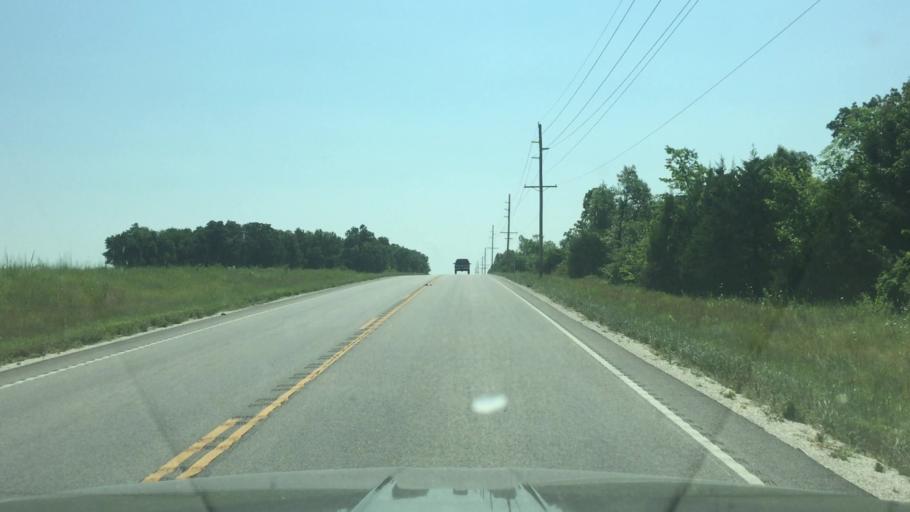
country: US
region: Missouri
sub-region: Miller County
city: Eldon
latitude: 38.3886
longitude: -92.7002
